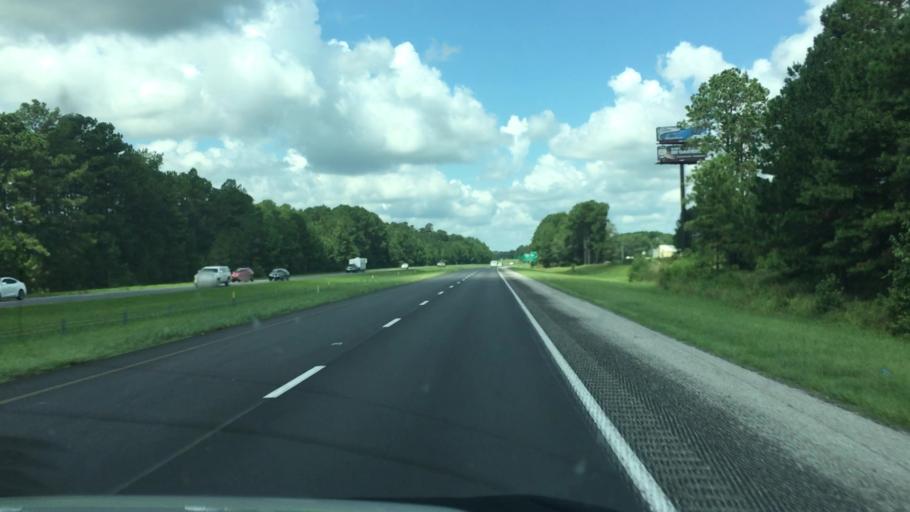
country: US
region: South Carolina
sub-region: Florence County
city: Timmonsville
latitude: 34.2054
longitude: -80.0151
